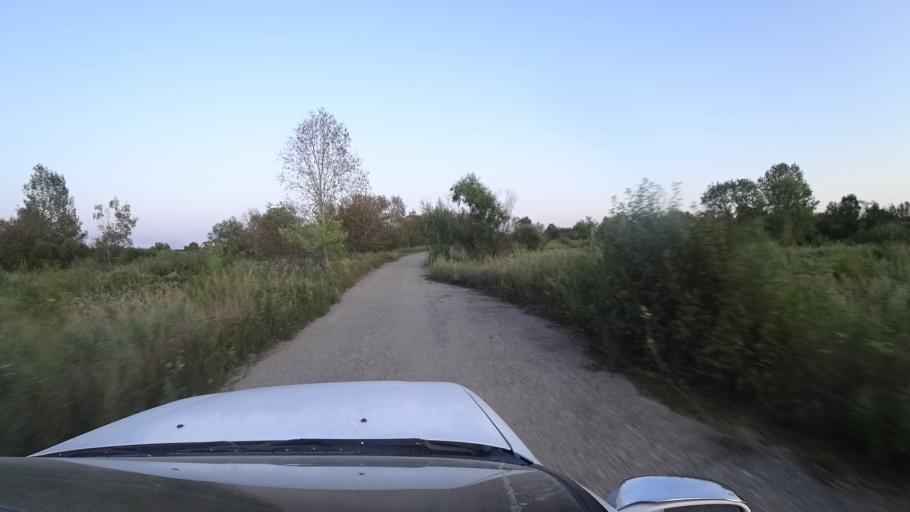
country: RU
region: Primorskiy
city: Dal'nerechensk
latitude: 45.9491
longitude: 133.7617
